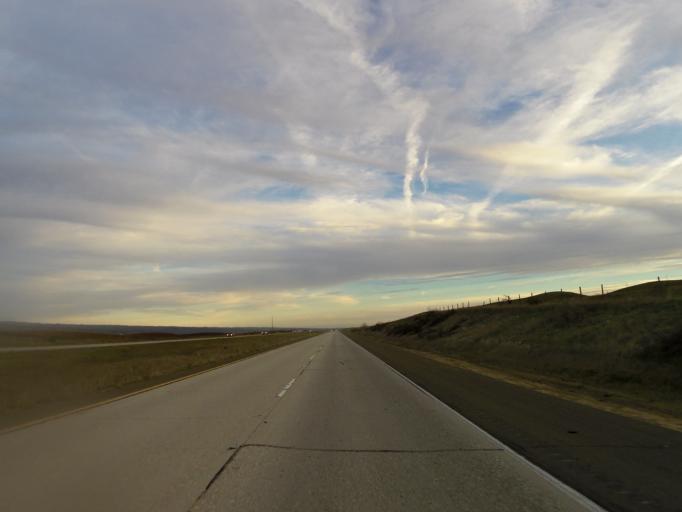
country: US
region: California
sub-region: Monterey County
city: King City
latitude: 36.0549
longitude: -120.9721
